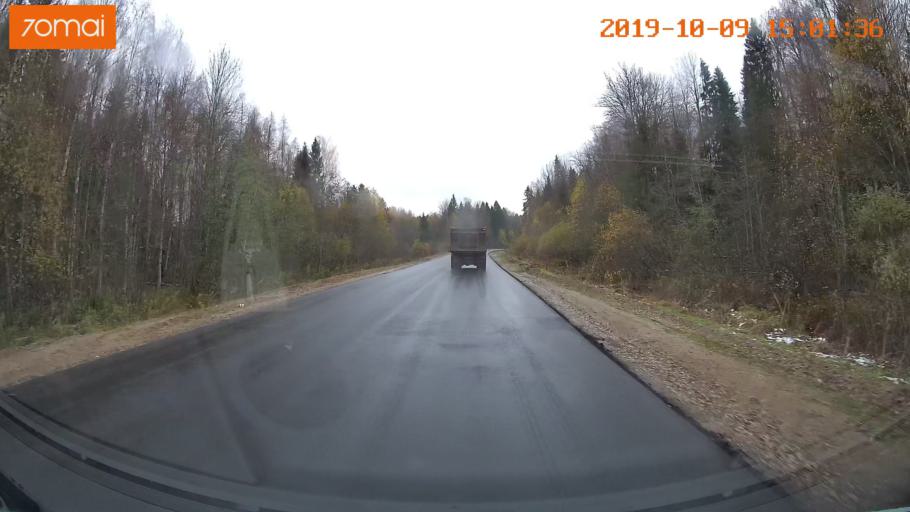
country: RU
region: Kostroma
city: Chistyye Bory
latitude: 58.2950
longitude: 41.6810
